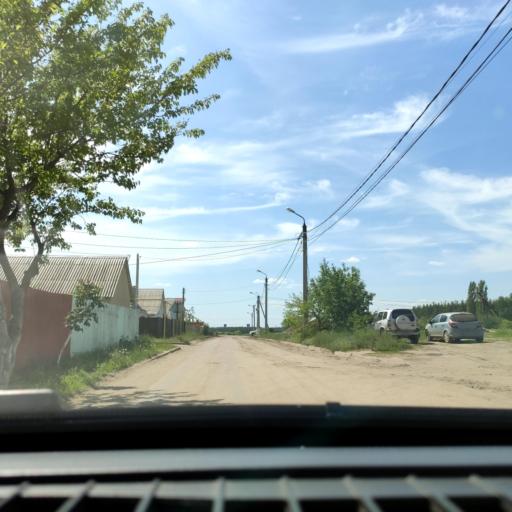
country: RU
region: Voronezj
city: Maslovka
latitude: 51.5848
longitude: 39.3121
